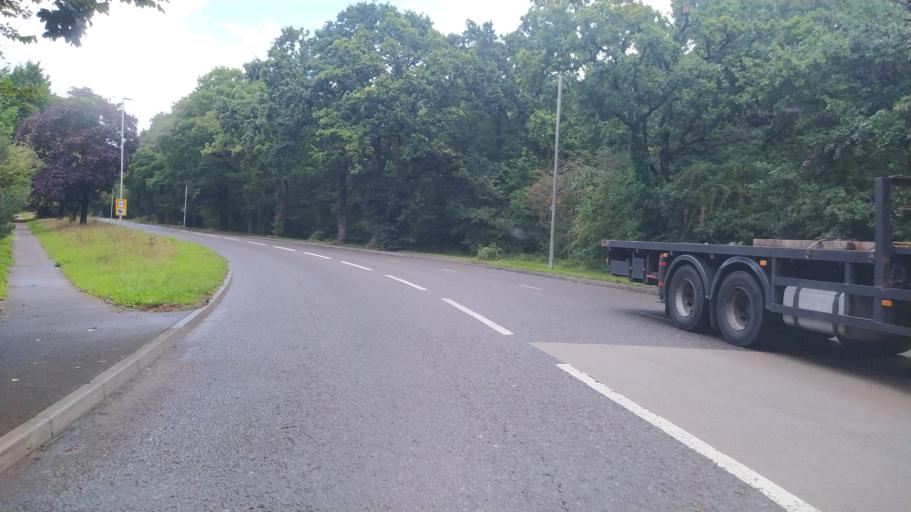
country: GB
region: England
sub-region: Dorset
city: Broadstone
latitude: 50.7511
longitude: -1.9833
